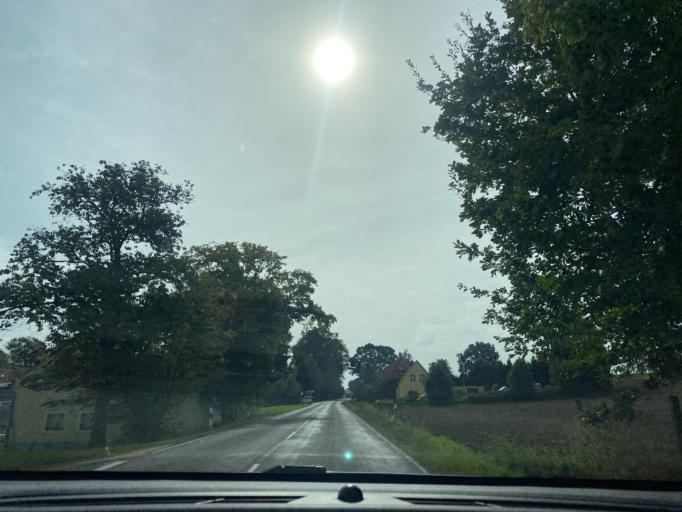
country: DE
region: Saxony
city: Reichenbach
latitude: 51.1614
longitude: 14.7921
